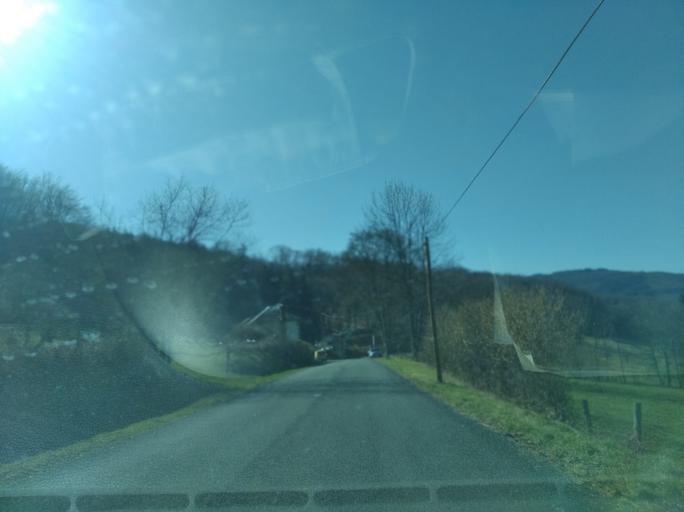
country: FR
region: Rhone-Alpes
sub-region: Departement de la Loire
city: Ambierle
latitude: 46.1083
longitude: 3.7867
